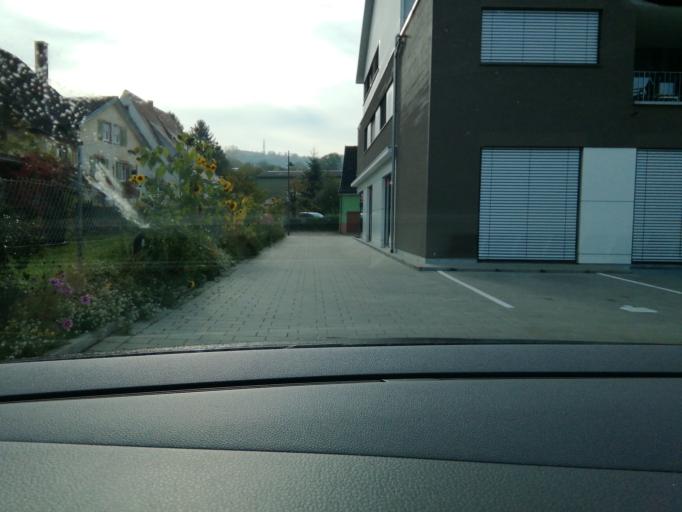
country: DE
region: Baden-Wuerttemberg
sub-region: Freiburg Region
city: Binzen
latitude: 47.6312
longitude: 7.6219
